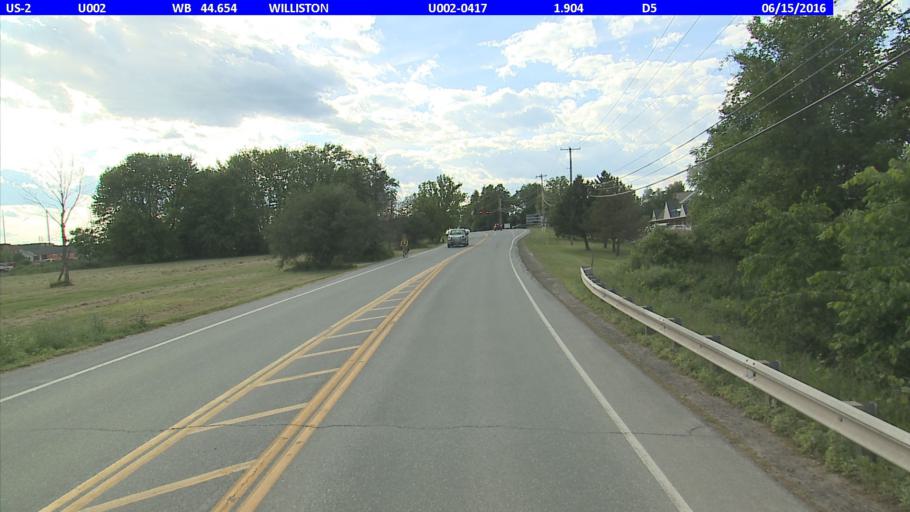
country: US
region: Vermont
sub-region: Chittenden County
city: Williston
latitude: 44.4456
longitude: -73.1028
